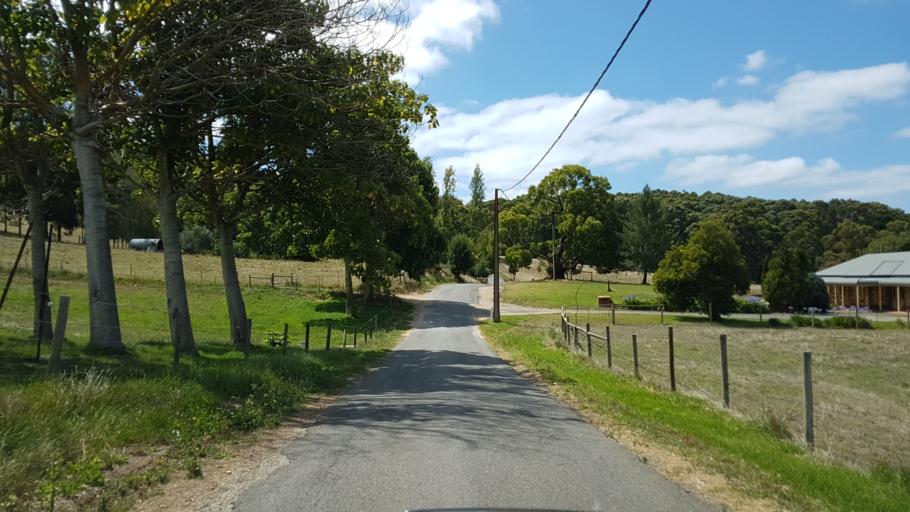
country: AU
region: South Australia
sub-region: Adelaide Hills
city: Crafers
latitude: -34.9751
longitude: 138.7174
